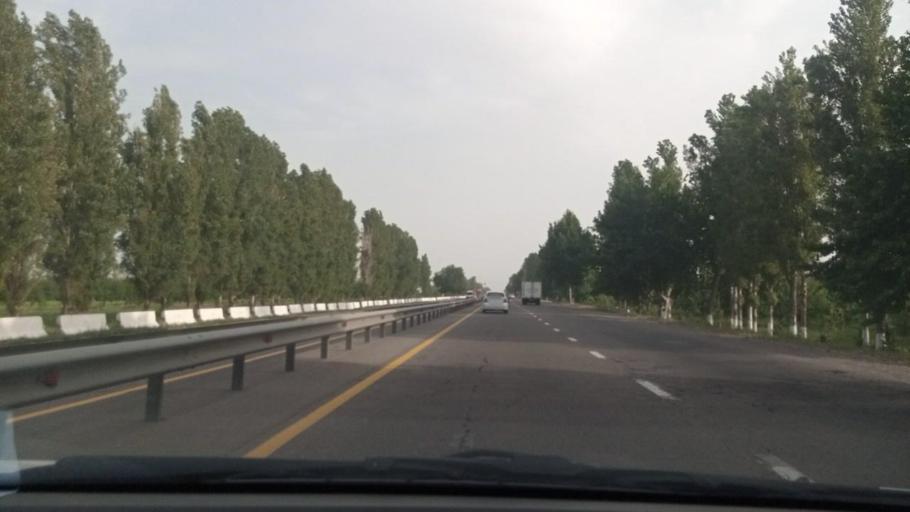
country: UZ
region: Toshkent Shahri
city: Bektemir
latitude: 41.2138
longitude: 69.4026
